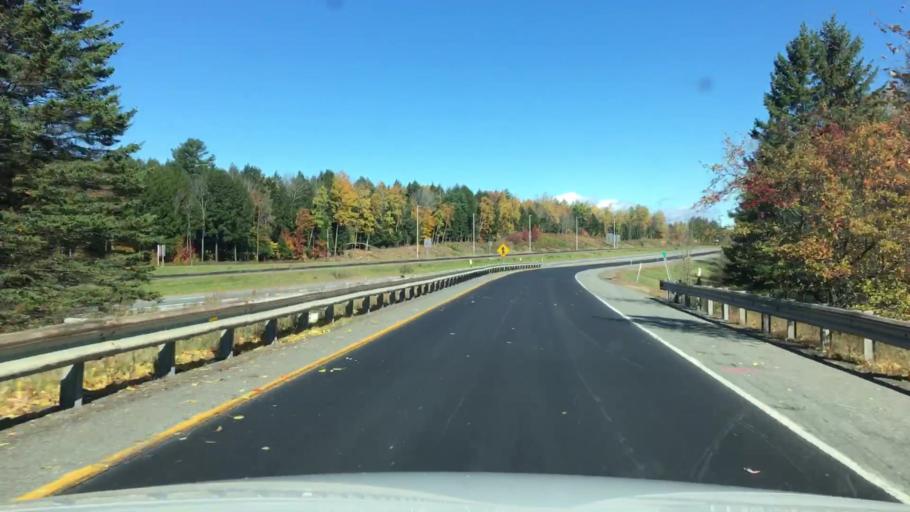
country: US
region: Maine
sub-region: Penobscot County
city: Medway
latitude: 45.6075
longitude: -68.5202
